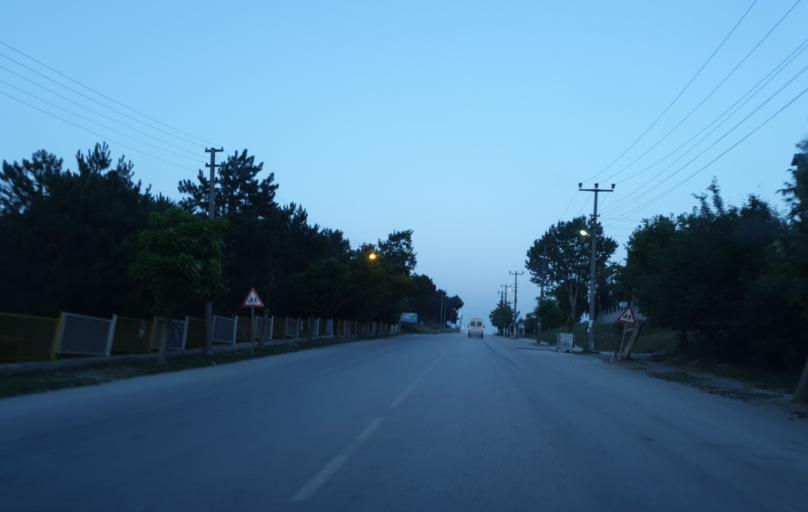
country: TR
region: Tekirdag
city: Saray
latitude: 41.3721
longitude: 27.9324
